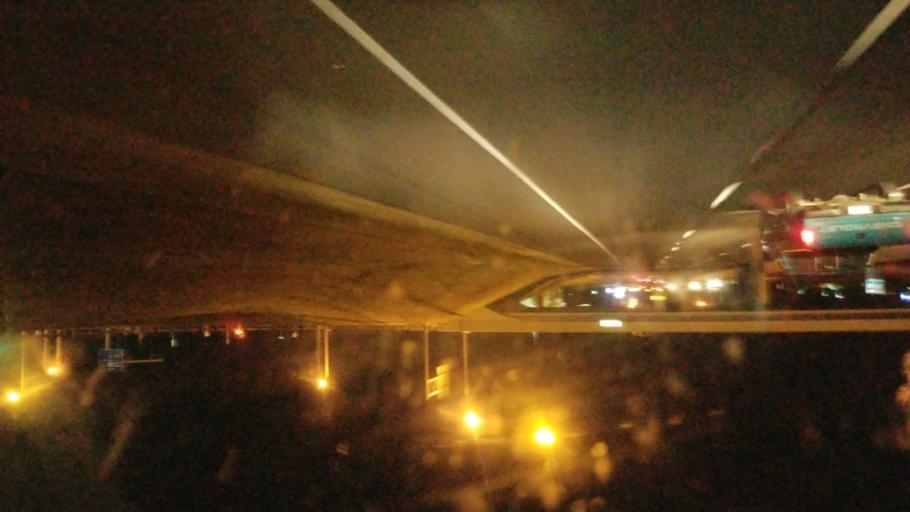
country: US
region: Indiana
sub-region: Allen County
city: Fort Wayne
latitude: 41.1780
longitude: -85.1032
